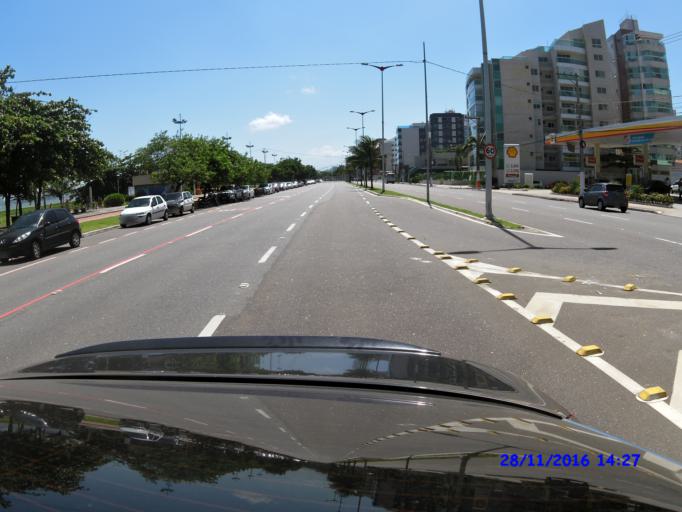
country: BR
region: Espirito Santo
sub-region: Vila Velha
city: Vila Velha
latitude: -20.2651
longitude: -40.2647
